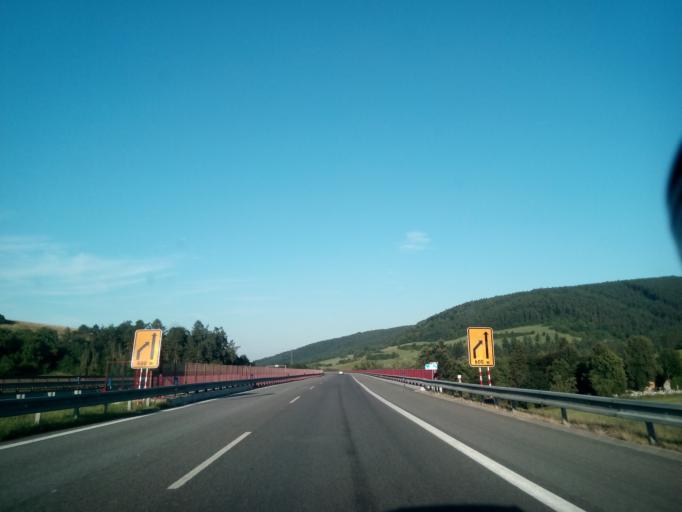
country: SK
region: Presovsky
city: Lipany
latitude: 49.0182
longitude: 20.9681
